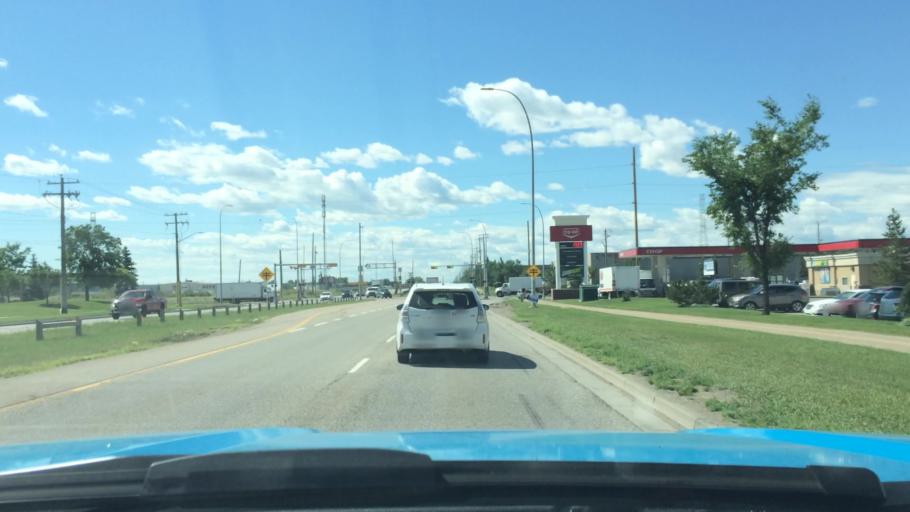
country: CA
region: Alberta
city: Calgary
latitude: 51.0102
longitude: -113.9588
